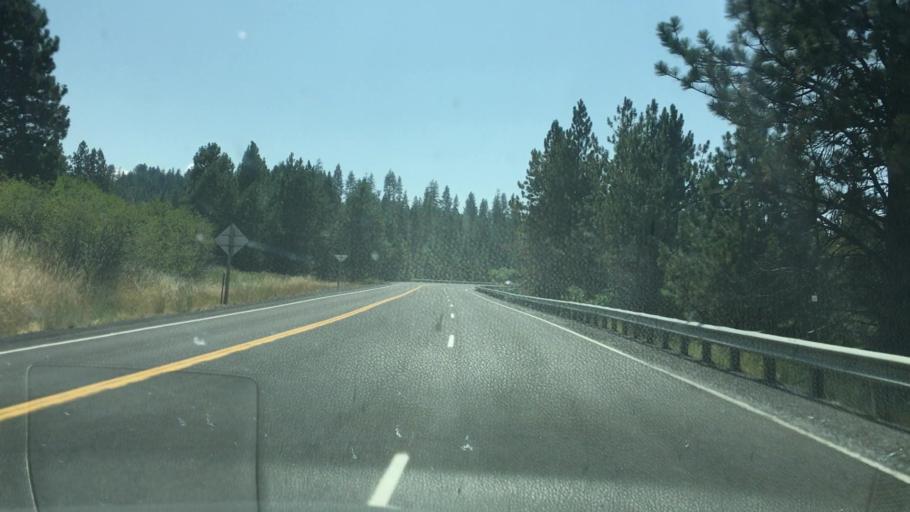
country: US
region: Idaho
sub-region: Idaho County
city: Grangeville
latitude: 45.8693
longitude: -116.2366
